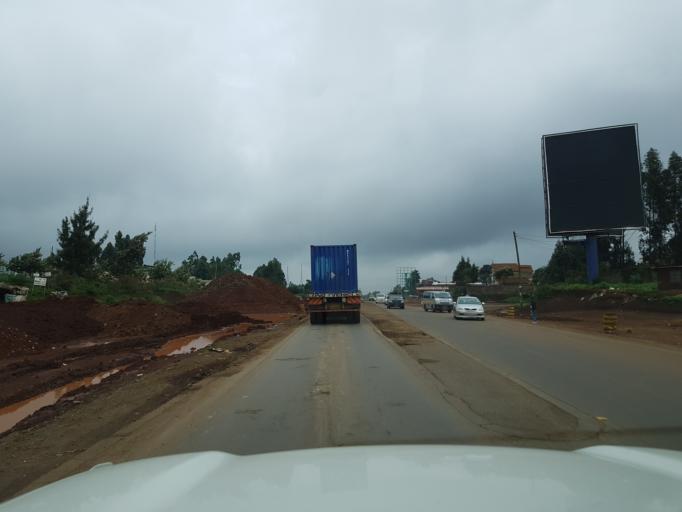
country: KE
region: Kiambu
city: Limuru
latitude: -1.1338
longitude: 36.6351
